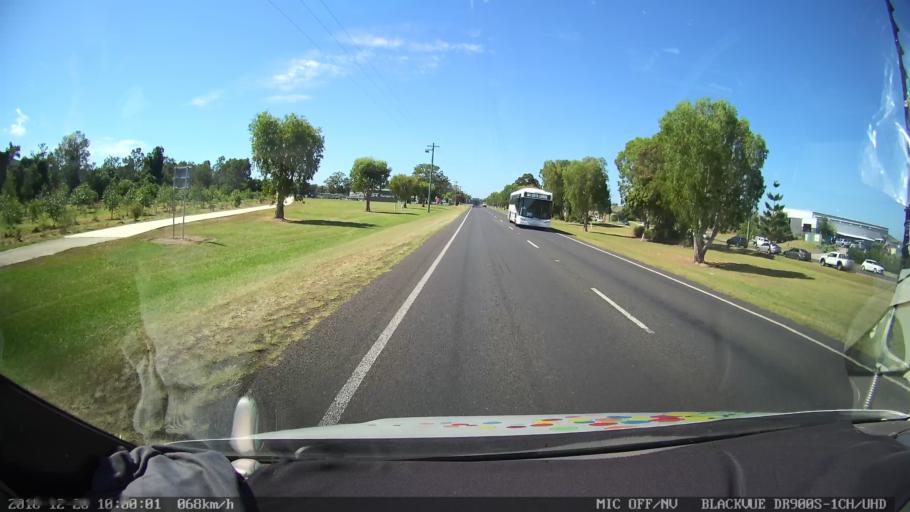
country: AU
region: New South Wales
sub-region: Lismore Municipality
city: Lismore
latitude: -28.8281
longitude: 153.2650
